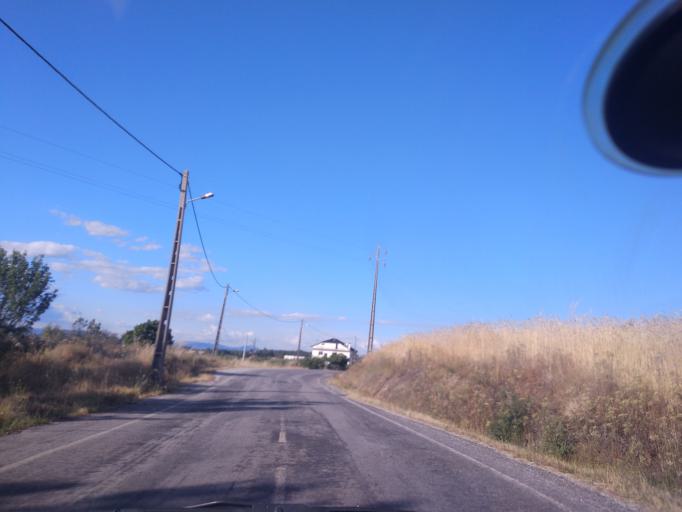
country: PT
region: Castelo Branco
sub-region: Covilha
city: Teixoso
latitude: 40.2488
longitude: -7.4083
